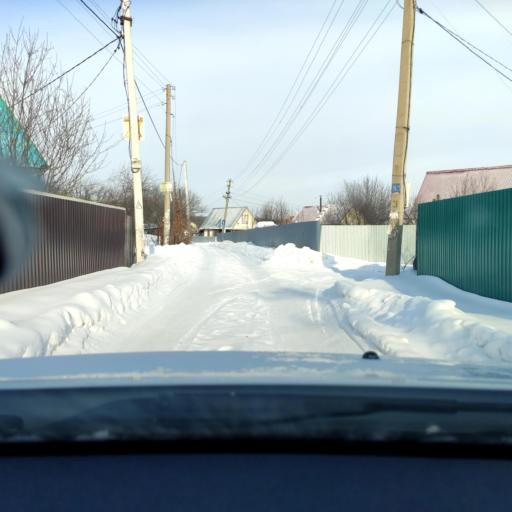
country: RU
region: Bashkortostan
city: Avdon
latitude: 54.7174
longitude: 55.7818
